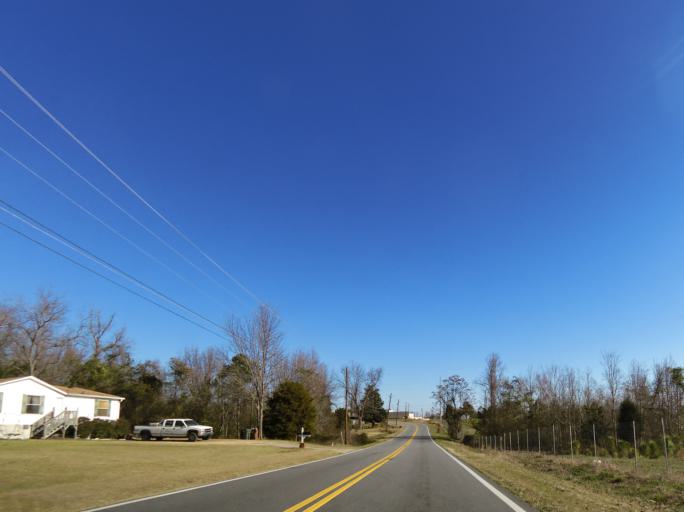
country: US
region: Georgia
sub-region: Bibb County
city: West Point
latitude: 32.8062
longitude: -83.7473
